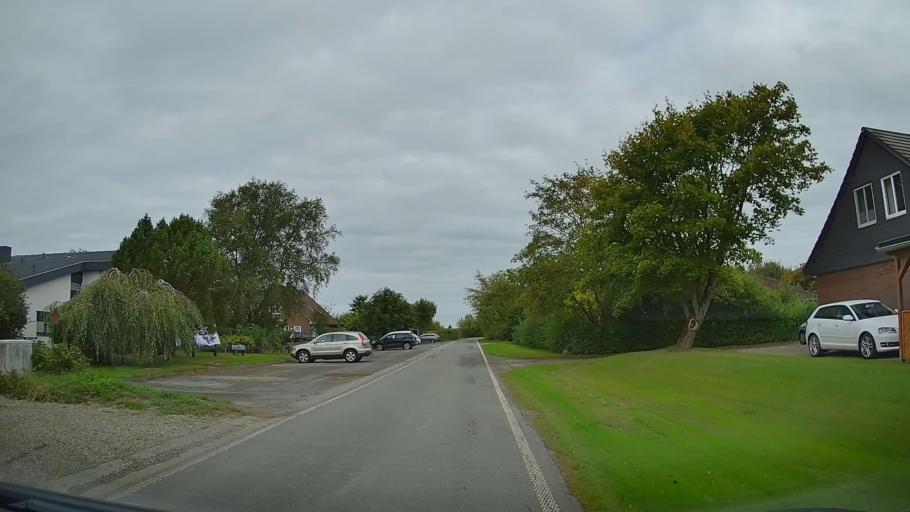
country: DE
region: Schleswig-Holstein
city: Rodenas
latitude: 54.8895
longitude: 8.7003
